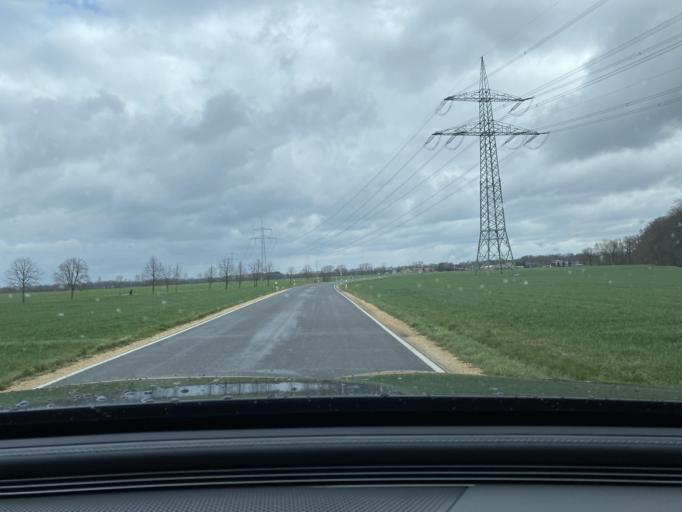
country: DE
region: Saxony
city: Grossdubrau
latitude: 51.2913
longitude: 14.4436
